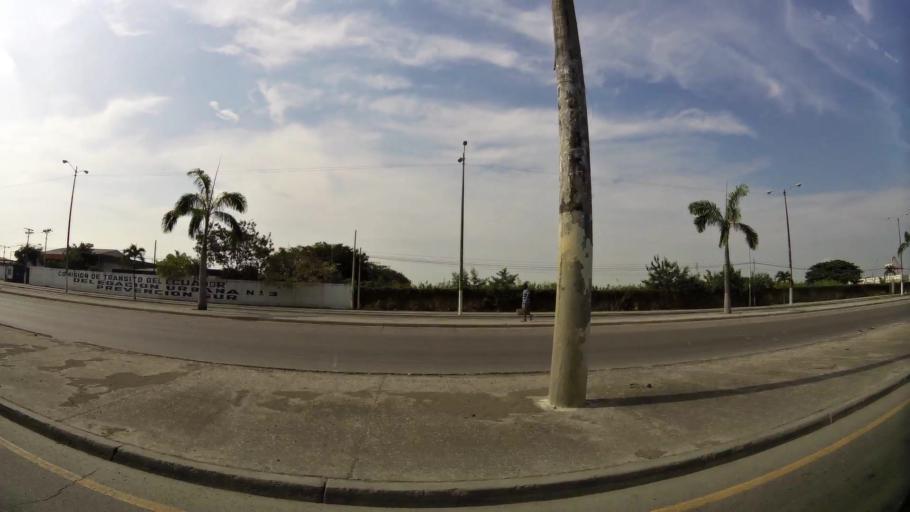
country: EC
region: Guayas
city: Guayaquil
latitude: -2.2730
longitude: -79.9045
